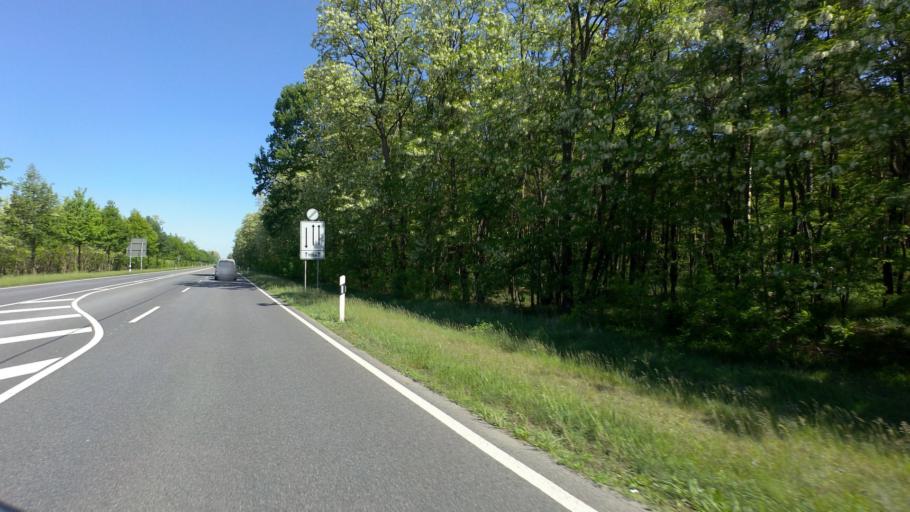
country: DE
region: Brandenburg
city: Spremberg
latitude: 51.6128
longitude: 14.3632
